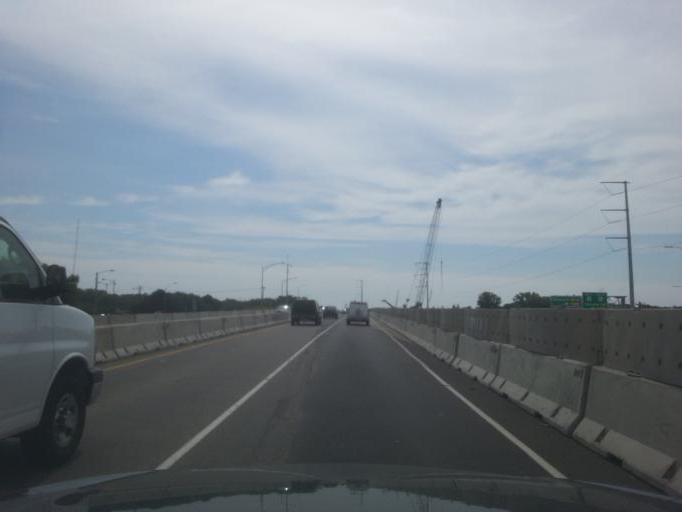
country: US
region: Wisconsin
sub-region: Dane County
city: Shorewood Hills
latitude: 43.0378
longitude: -89.4553
